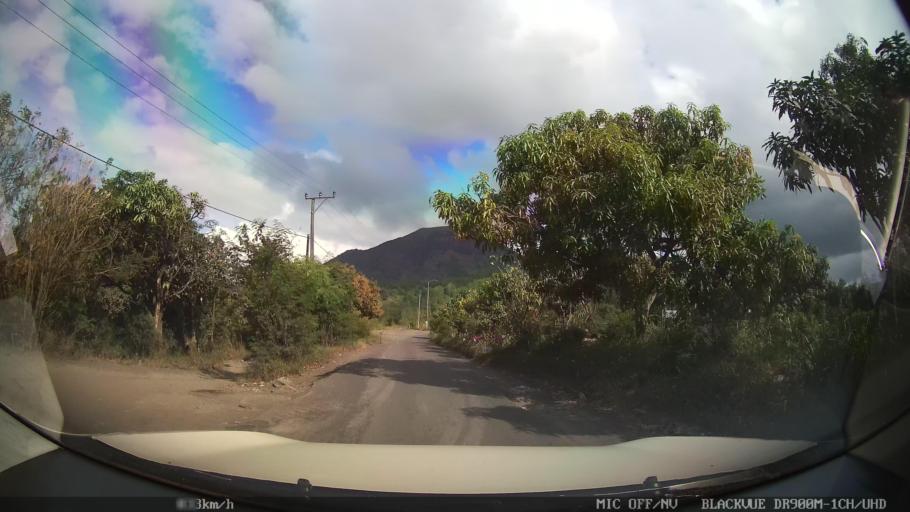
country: ID
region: Bali
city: Banjar Kedisan
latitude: -8.2178
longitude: 115.3640
